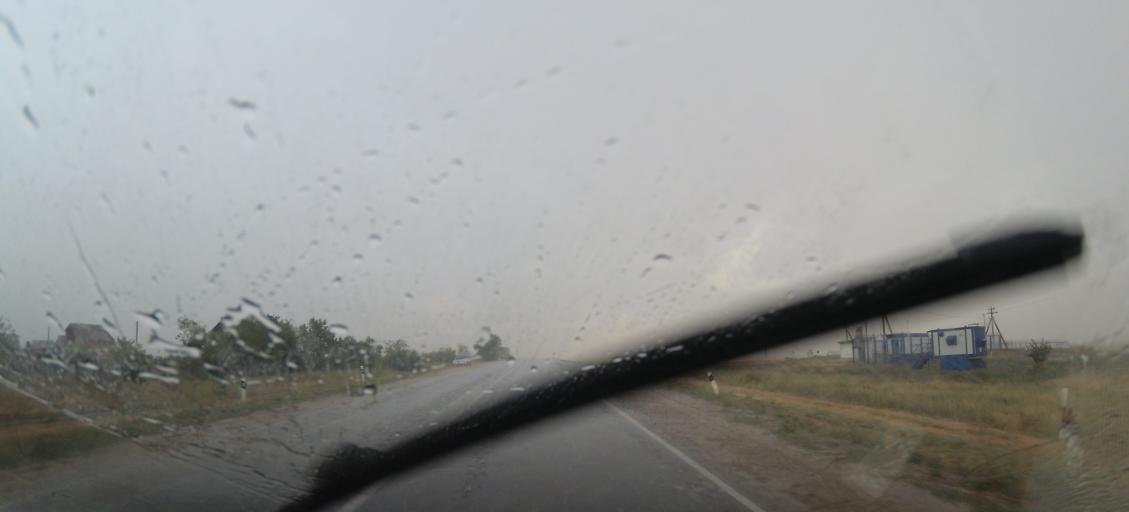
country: RU
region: Rostov
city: Proletarsk
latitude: 46.6806
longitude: 41.7125
